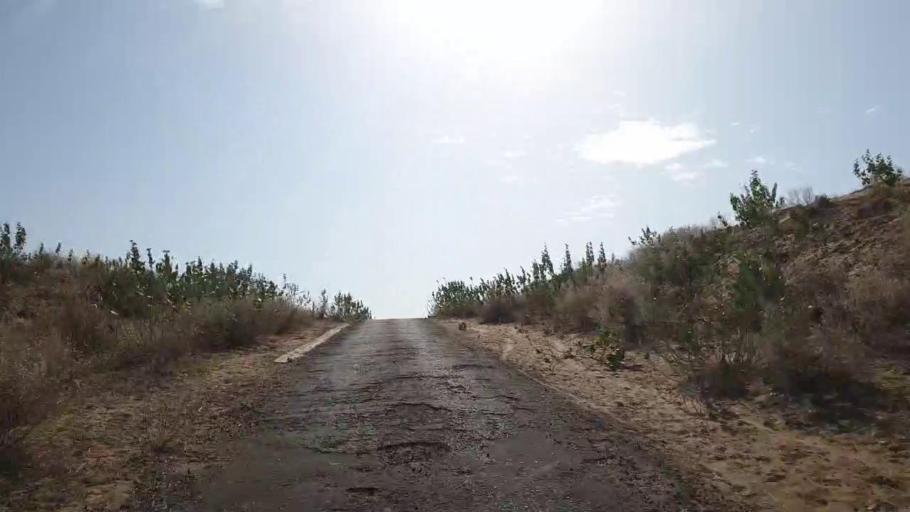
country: PK
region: Sindh
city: Islamkot
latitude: 25.0610
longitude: 70.0315
